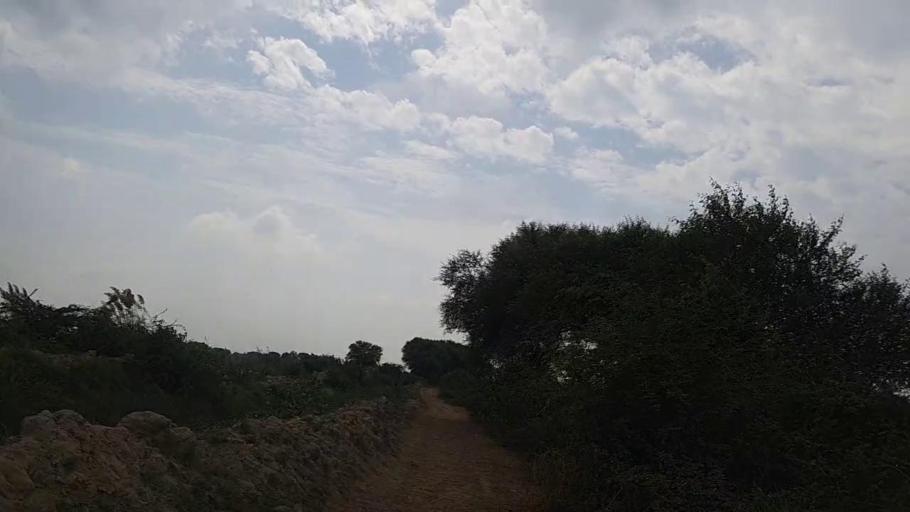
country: PK
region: Sindh
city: Mirpur Batoro
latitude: 24.6161
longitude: 68.1359
